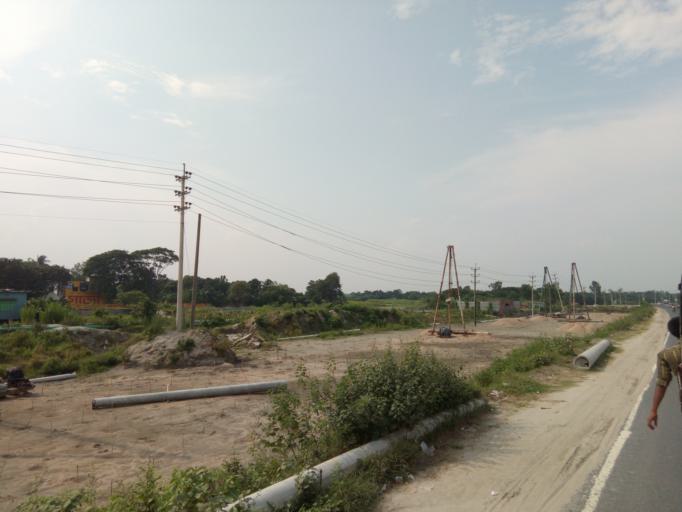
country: BD
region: Dhaka
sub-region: Dhaka
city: Dhaka
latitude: 23.6526
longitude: 90.3510
